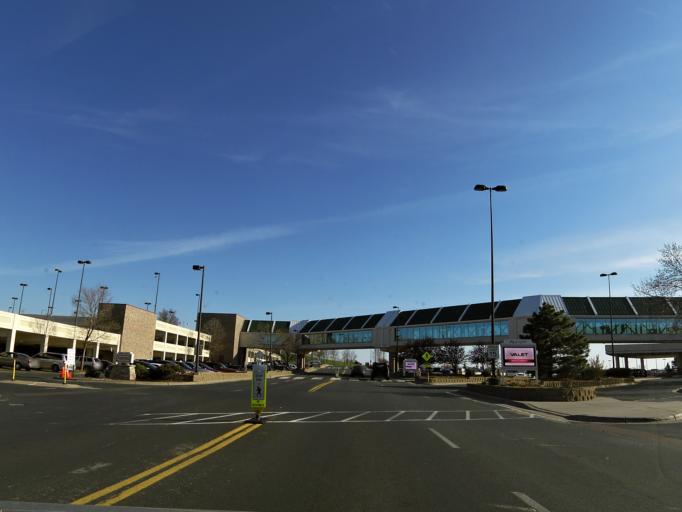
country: US
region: Minnesota
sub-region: Scott County
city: Prior Lake
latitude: 44.7313
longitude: -93.4715
